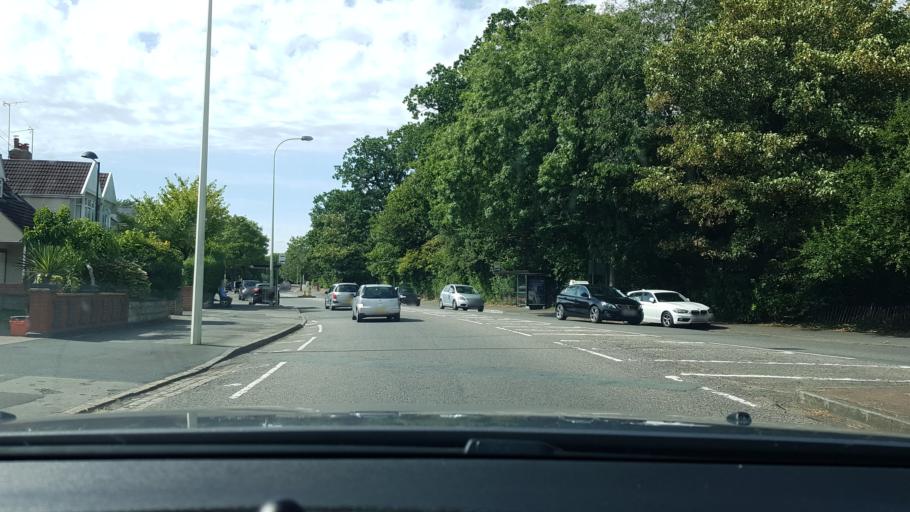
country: GB
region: England
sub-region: Borough of Swindon
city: Swindon
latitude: 51.5440
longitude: -1.7663
